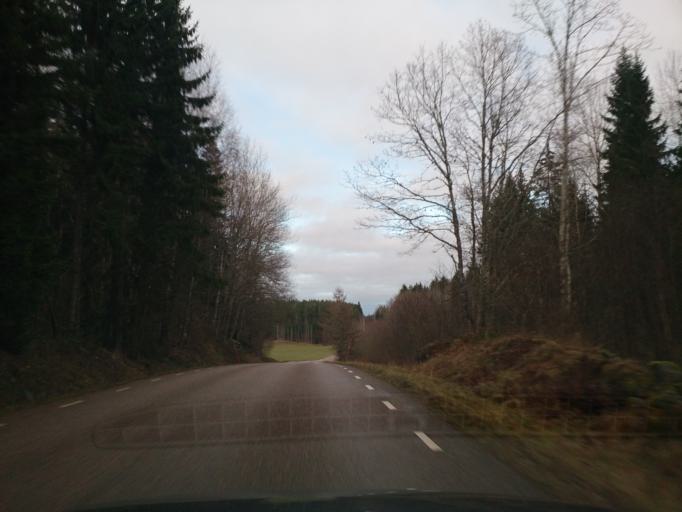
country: SE
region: OEstergoetland
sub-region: Atvidabergs Kommun
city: Atvidaberg
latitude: 58.2982
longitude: 16.0089
